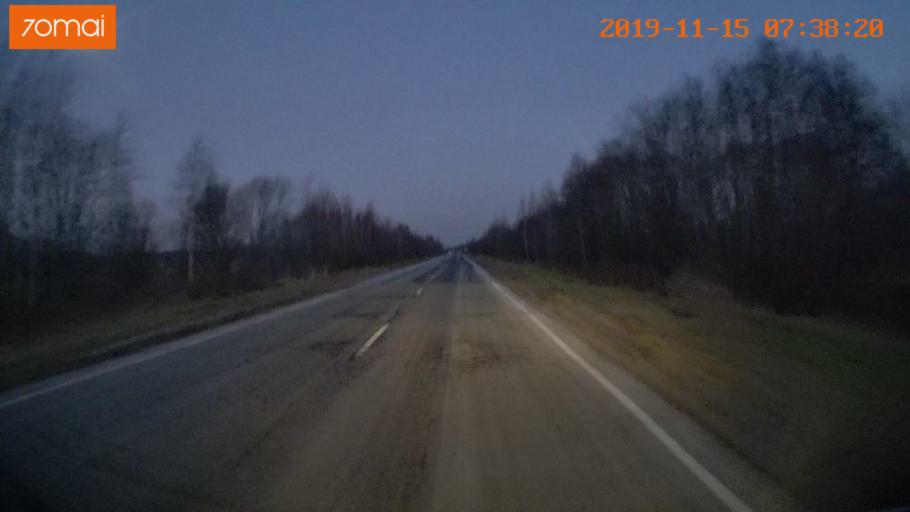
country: RU
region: Vologda
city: Sheksna
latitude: 58.7550
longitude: 38.4060
